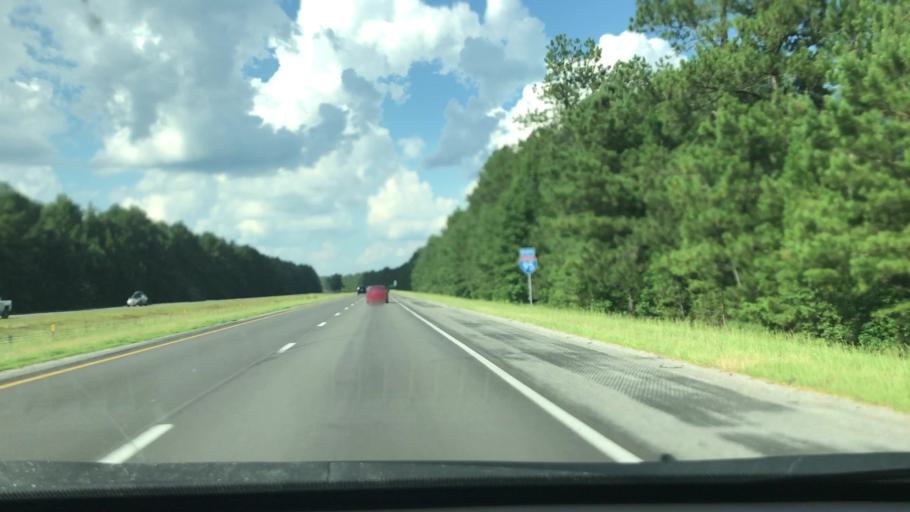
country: US
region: South Carolina
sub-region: Sumter County
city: East Sumter
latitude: 33.8658
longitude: -80.1089
